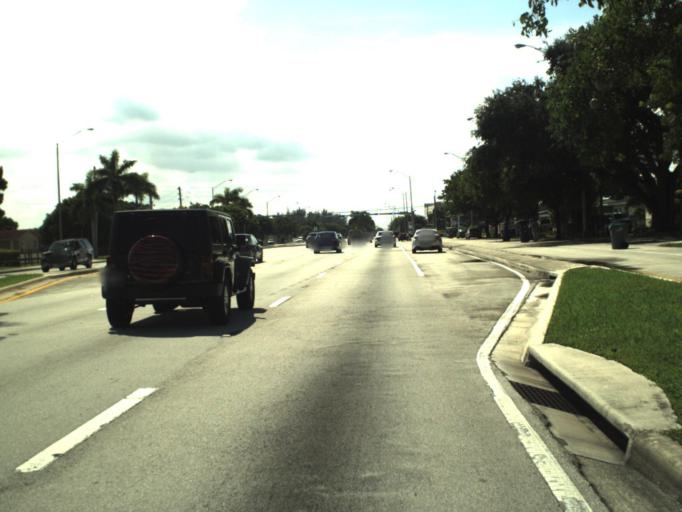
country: US
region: Florida
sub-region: Miami-Dade County
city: Carol City
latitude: 25.9408
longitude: -80.2514
